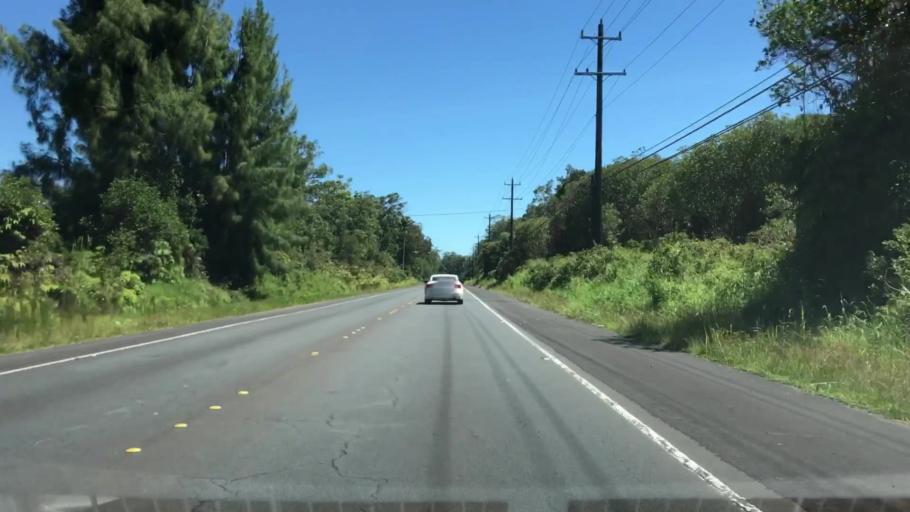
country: US
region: Hawaii
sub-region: Hawaii County
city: Fern Acres
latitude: 19.4903
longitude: -155.1499
